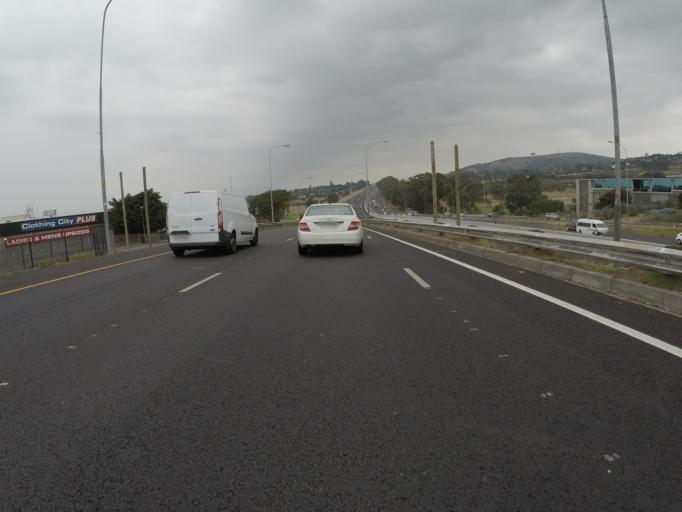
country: ZA
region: Western Cape
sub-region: City of Cape Town
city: Kraaifontein
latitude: -33.8877
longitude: 18.6324
